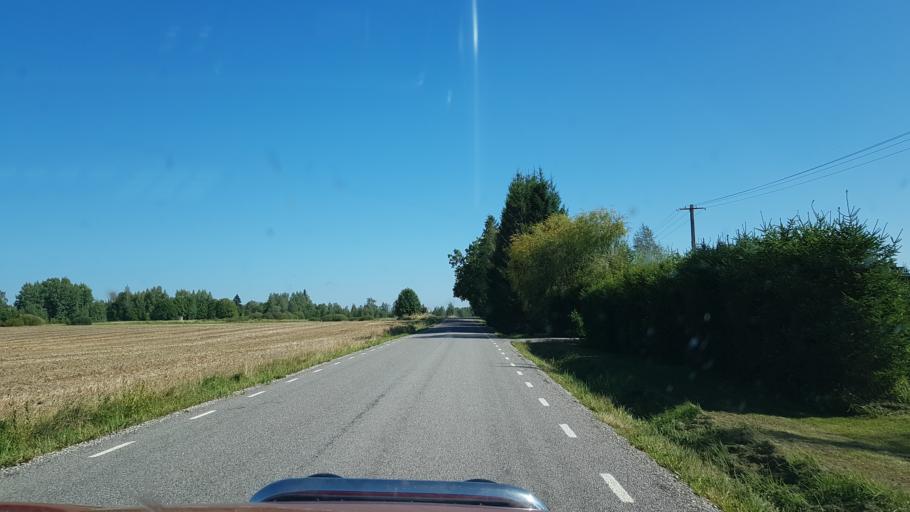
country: EE
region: Polvamaa
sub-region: Polva linn
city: Polva
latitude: 58.2131
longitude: 27.1793
